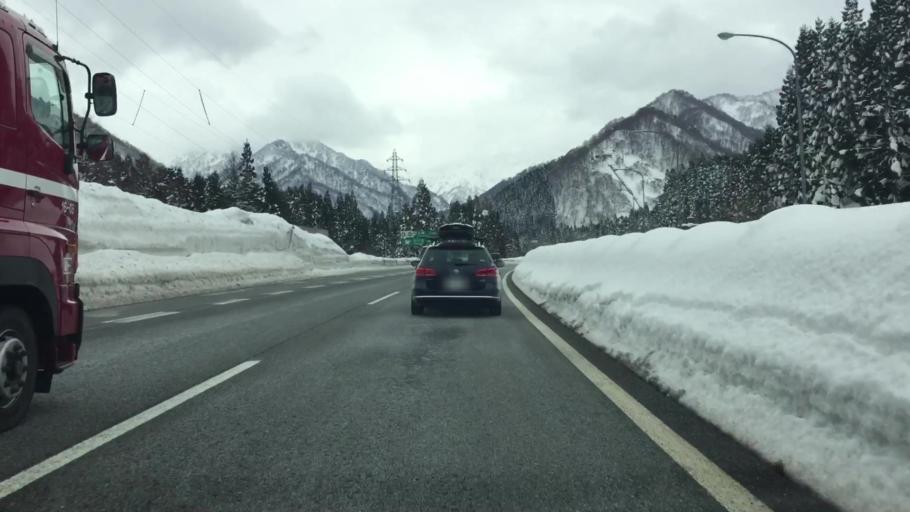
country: JP
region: Niigata
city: Shiozawa
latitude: 36.8853
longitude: 138.8511
